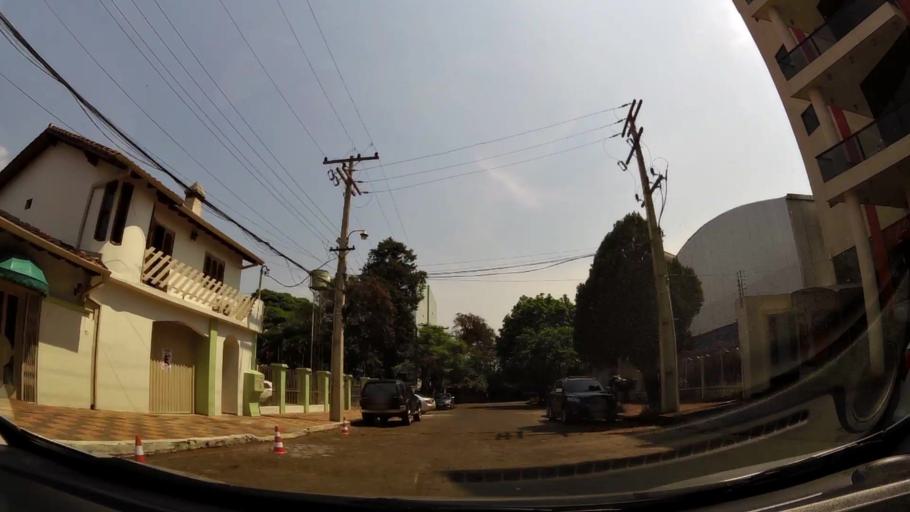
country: PY
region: Alto Parana
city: Ciudad del Este
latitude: -25.5168
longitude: -54.6160
